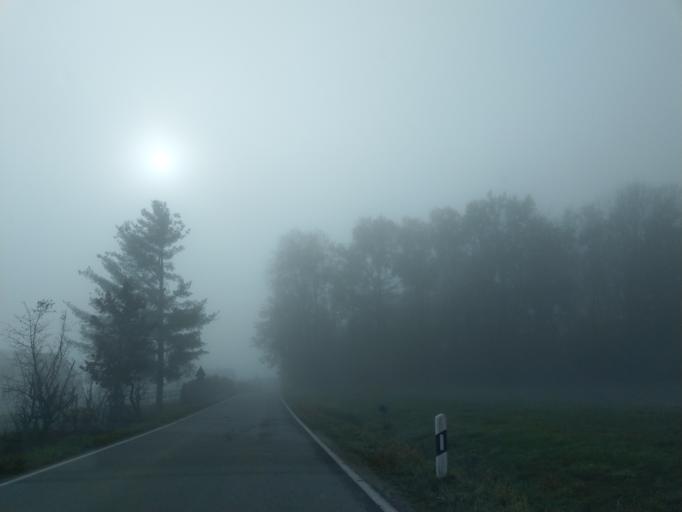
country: DE
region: Bavaria
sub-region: Lower Bavaria
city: Iggensbach
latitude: 48.7655
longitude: 13.1421
